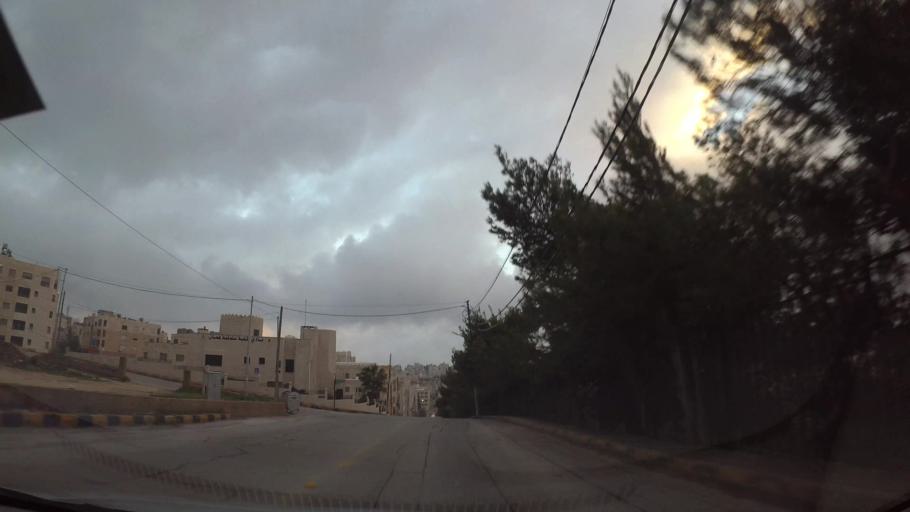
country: JO
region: Amman
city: Al Jubayhah
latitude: 32.0094
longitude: 35.8789
